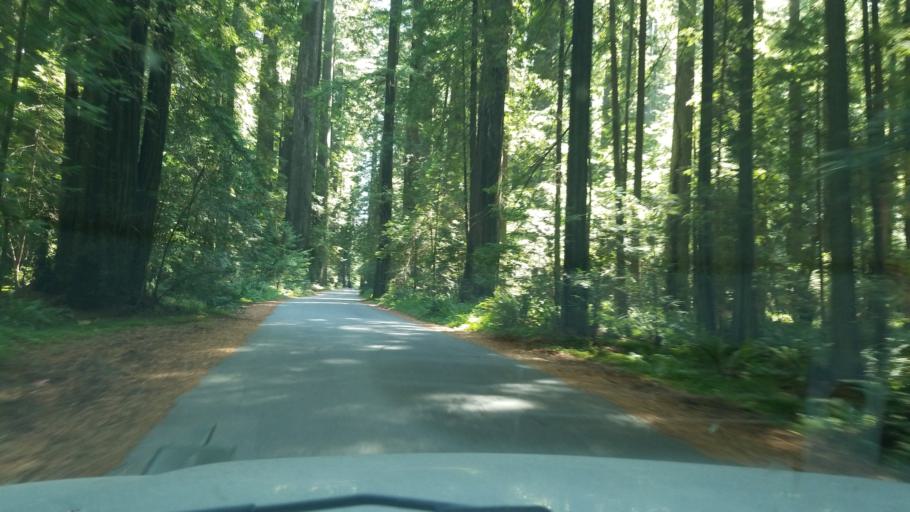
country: US
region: California
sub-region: Humboldt County
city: Rio Dell
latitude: 40.3516
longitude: -123.9216
